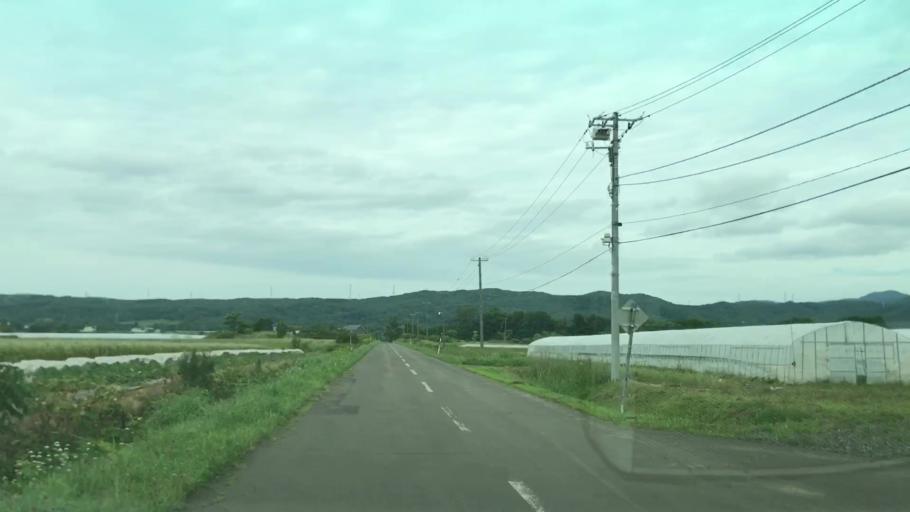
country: JP
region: Hokkaido
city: Iwanai
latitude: 43.0309
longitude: 140.5711
